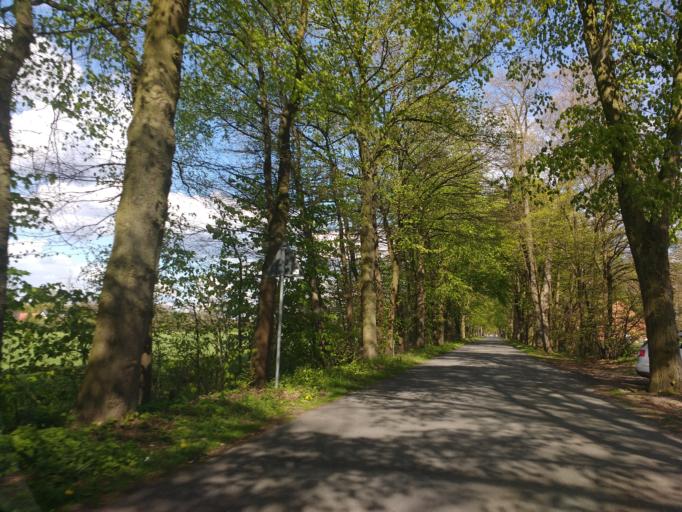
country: DE
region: North Rhine-Westphalia
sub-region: Regierungsbezirk Detmold
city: Hovelhof
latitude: 51.7880
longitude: 8.6875
